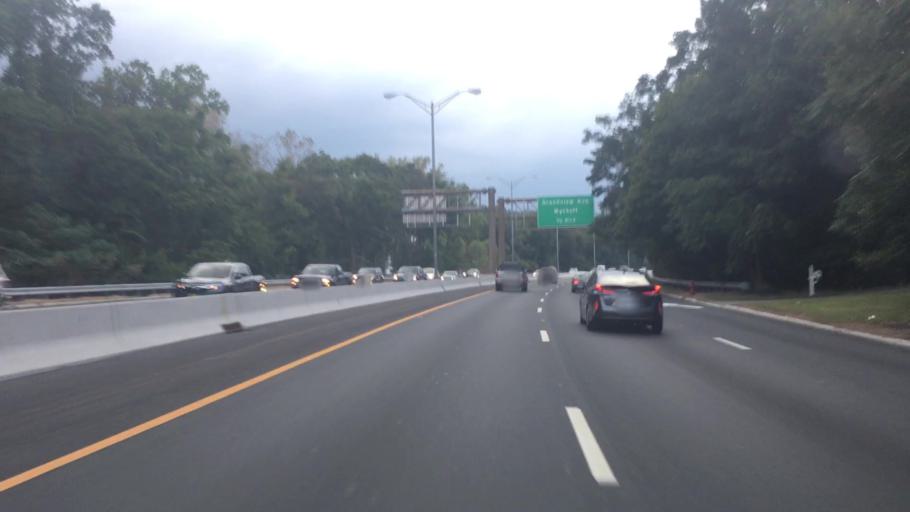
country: US
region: New Jersey
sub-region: Passaic County
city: Hawthorne
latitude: 40.9718
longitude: -74.1588
